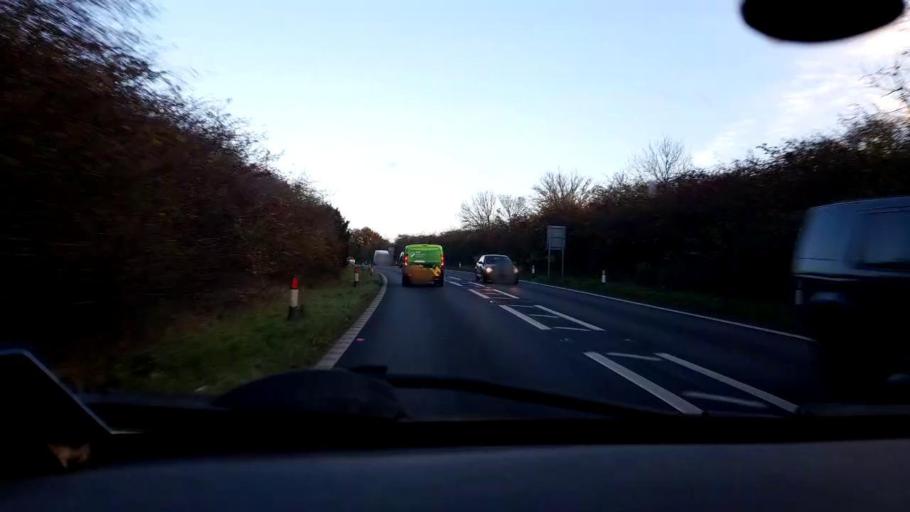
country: GB
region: England
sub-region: Norfolk
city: Hethersett
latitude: 52.6564
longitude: 1.1325
